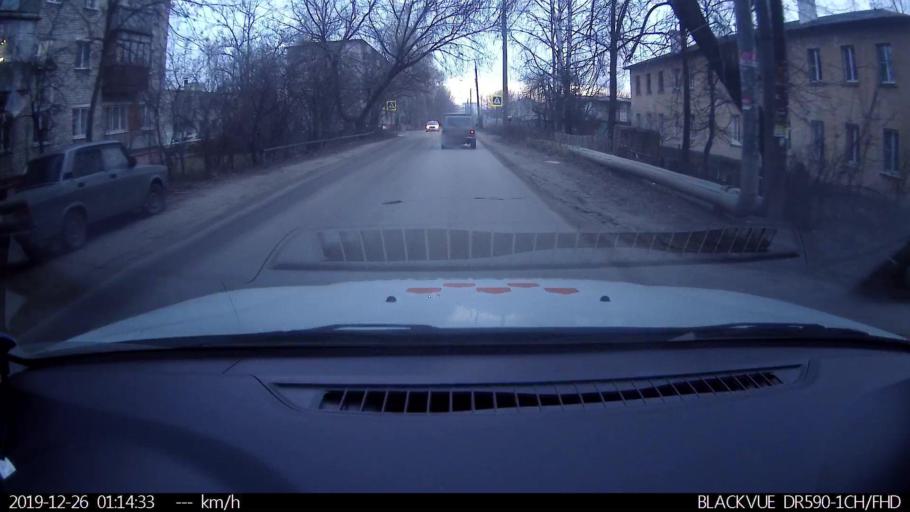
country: RU
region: Nizjnij Novgorod
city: Nizhniy Novgorod
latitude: 56.2734
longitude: 43.9095
